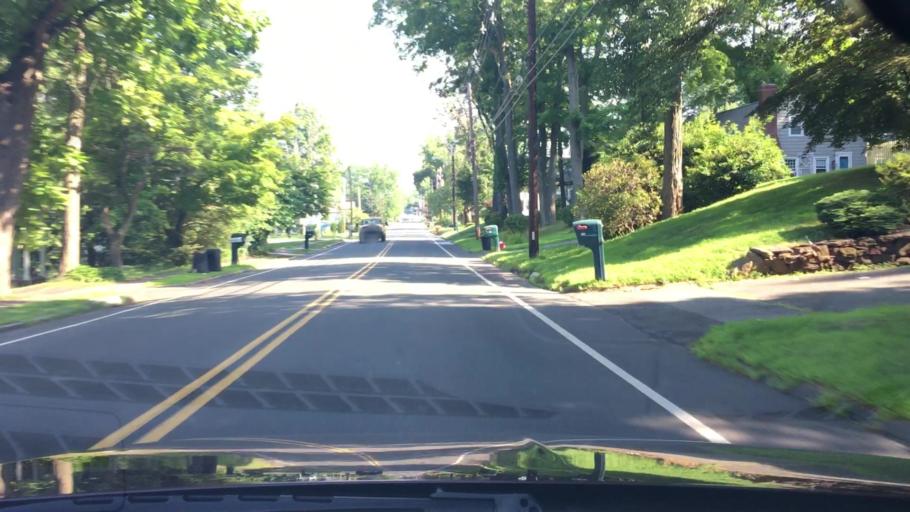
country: US
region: Massachusetts
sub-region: Hampden County
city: East Longmeadow
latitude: 42.0596
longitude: -72.5120
